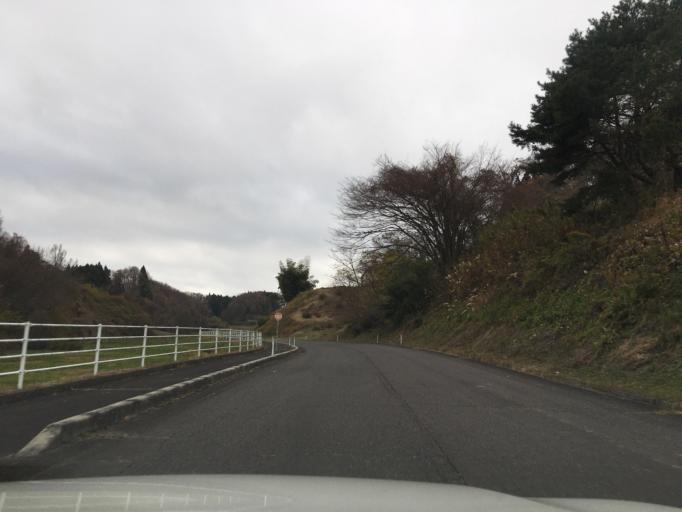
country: JP
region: Fukushima
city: Funehikimachi-funehiki
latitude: 37.4724
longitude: 140.5477
